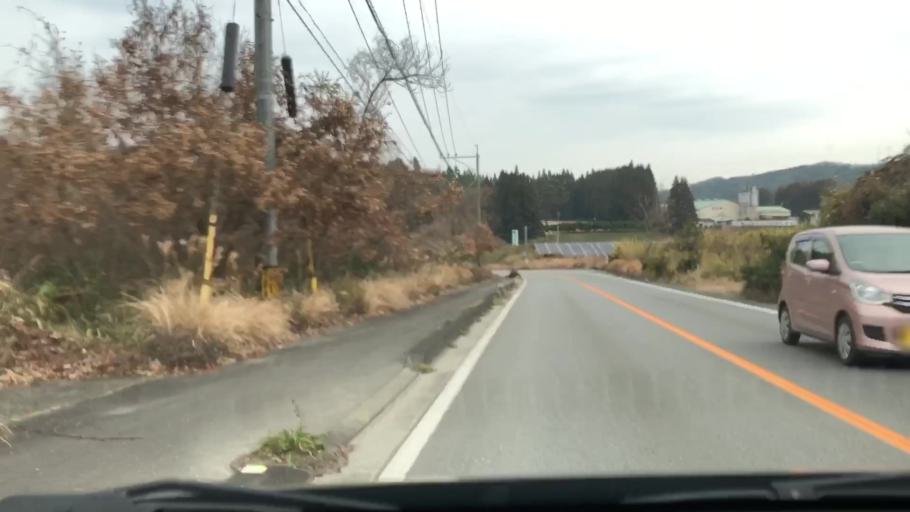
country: JP
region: Oita
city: Usuki
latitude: 33.0067
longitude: 131.6306
